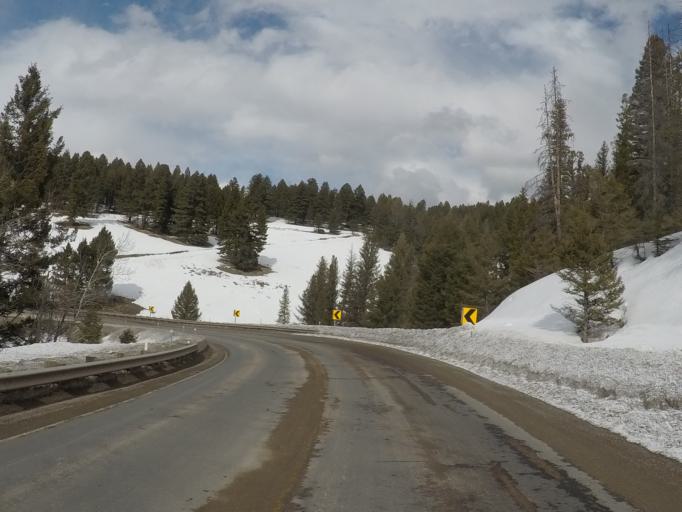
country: US
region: Montana
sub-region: Granite County
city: Philipsburg
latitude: 46.2275
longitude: -113.2881
